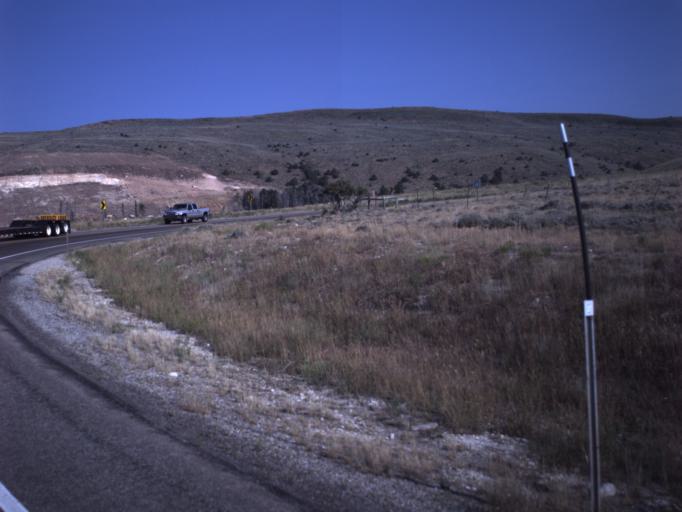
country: US
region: Utah
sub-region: Uintah County
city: Vernal
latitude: 40.6412
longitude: -109.4868
